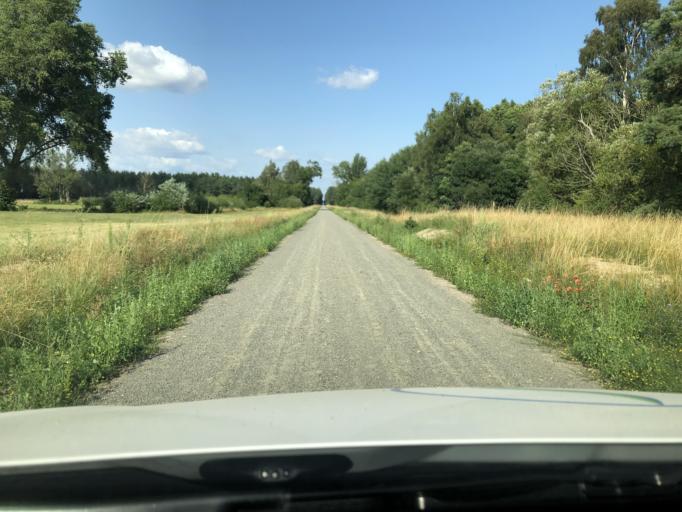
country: SE
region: Skane
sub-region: Kristianstads Kommun
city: Norra Asum
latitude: 55.9116
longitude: 14.1135
